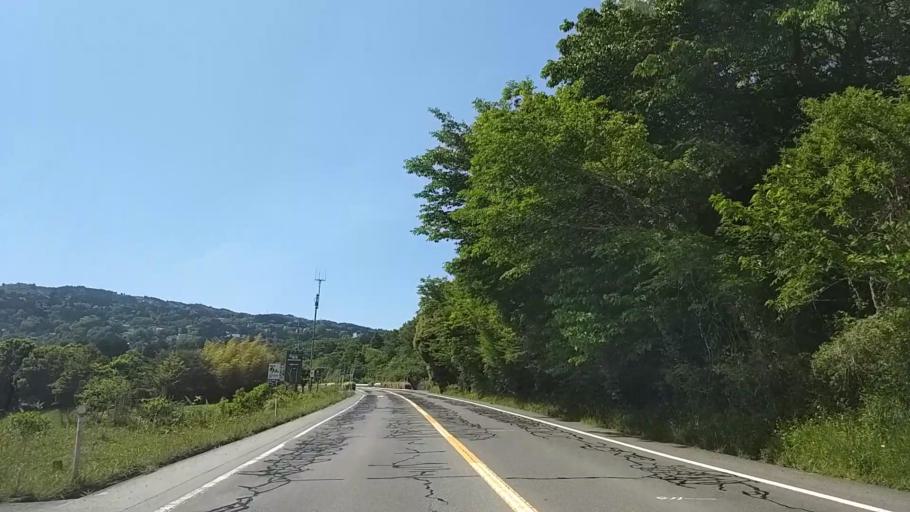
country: JP
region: Shizuoka
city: Atami
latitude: 35.0981
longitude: 139.0094
